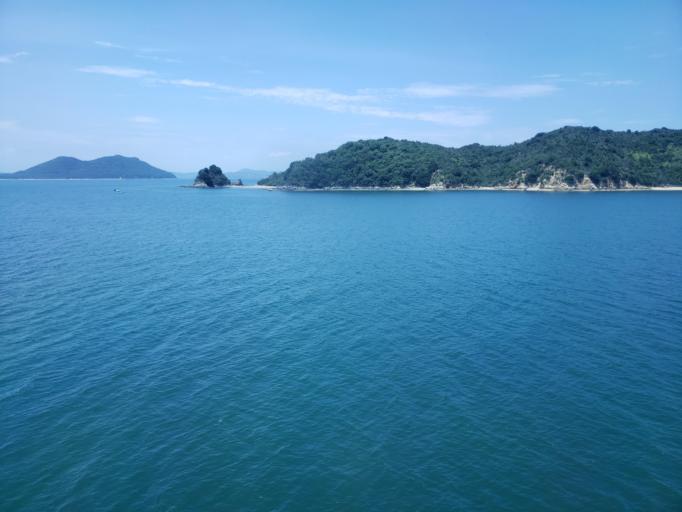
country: JP
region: Kagawa
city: Takamatsu-shi
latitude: 34.3958
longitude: 134.1041
